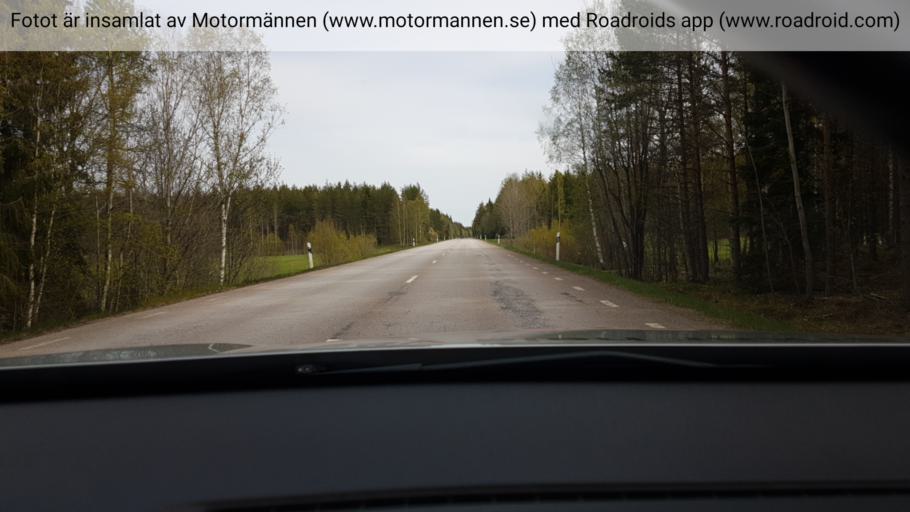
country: SE
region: Uppsala
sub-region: Tierps Kommun
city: Orbyhus
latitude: 60.2128
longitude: 17.7614
